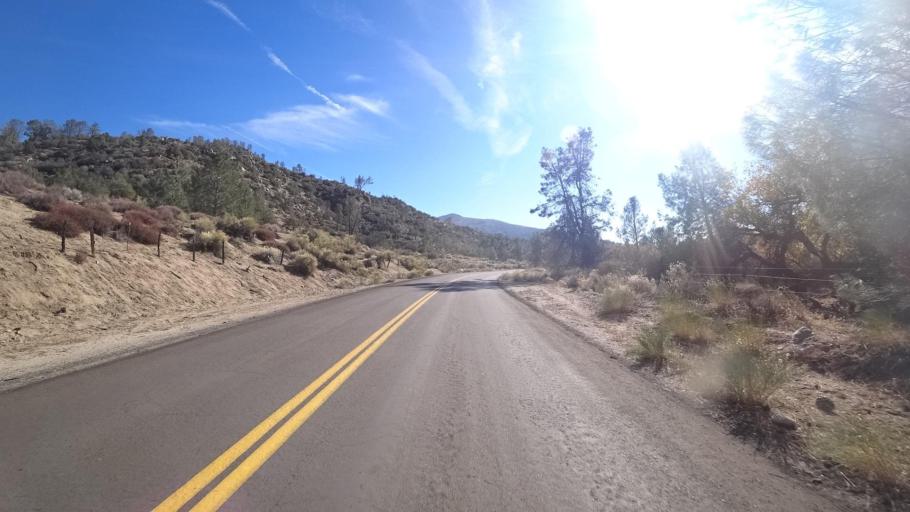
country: US
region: California
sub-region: Kern County
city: Bodfish
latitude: 35.5268
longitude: -118.5117
